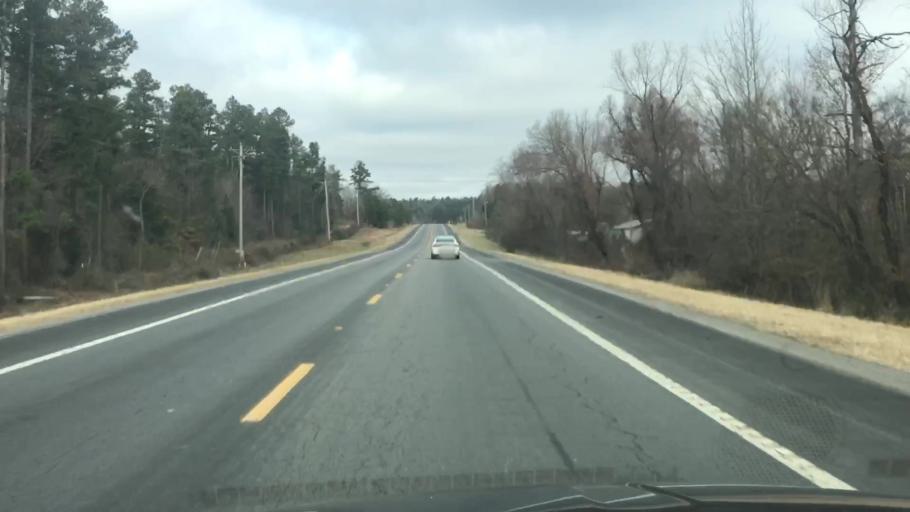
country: US
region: Arkansas
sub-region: Scott County
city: Waldron
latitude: 34.8312
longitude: -94.0417
